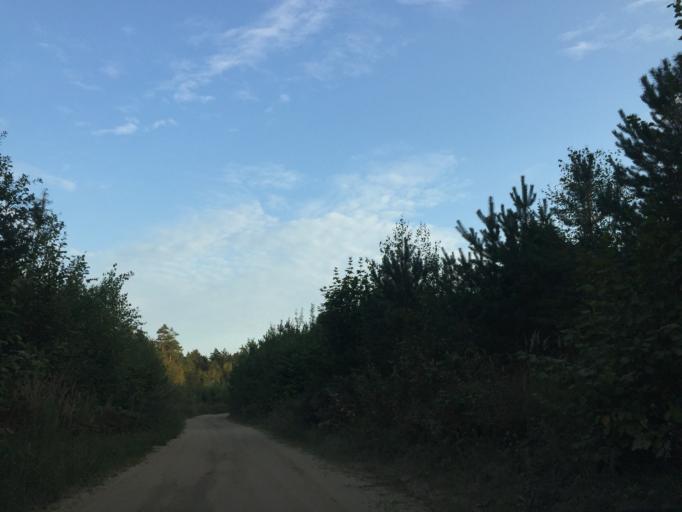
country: LV
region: Baldone
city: Baldone
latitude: 56.7645
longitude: 24.4077
